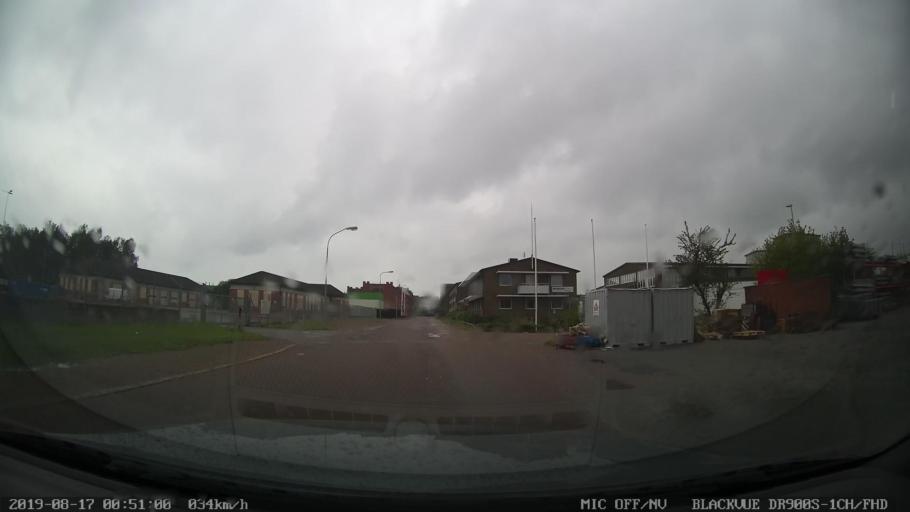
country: SE
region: Skane
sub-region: Landskrona
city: Landskrona
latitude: 55.8676
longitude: 12.8405
